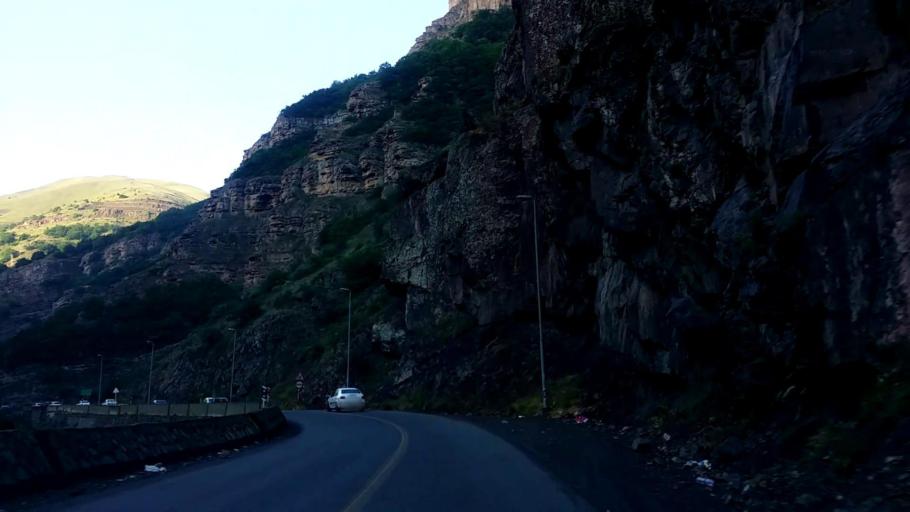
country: IR
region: Tehran
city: Tajrish
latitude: 36.2079
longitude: 51.3294
